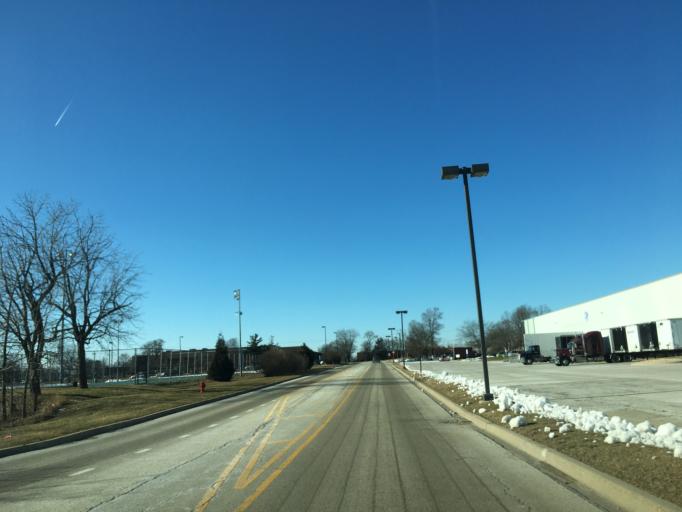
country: US
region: Illinois
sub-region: DuPage County
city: Wood Dale
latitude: 41.9791
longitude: -87.9771
